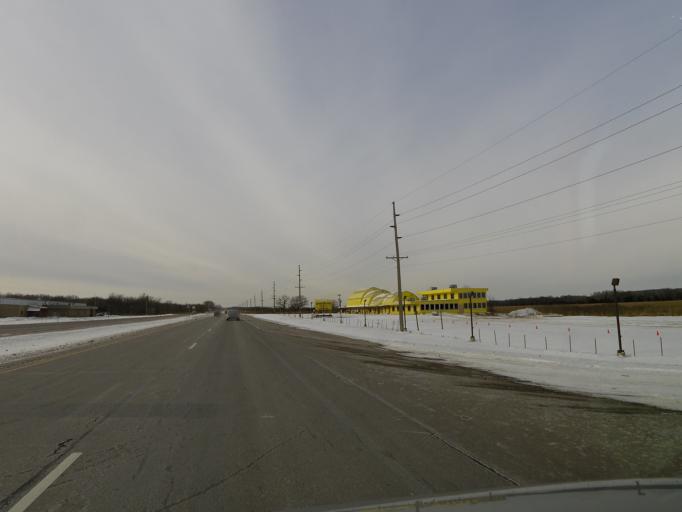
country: US
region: Minnesota
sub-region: Scott County
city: Jordan
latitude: 44.6545
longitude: -93.6827
